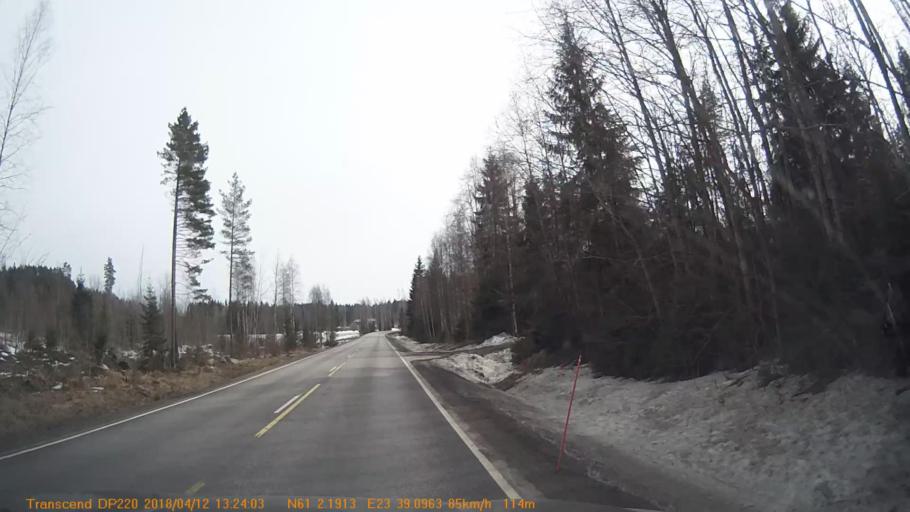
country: FI
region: Pirkanmaa
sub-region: Etelae-Pirkanmaa
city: Kylmaekoski
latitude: 61.0355
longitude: 23.6532
